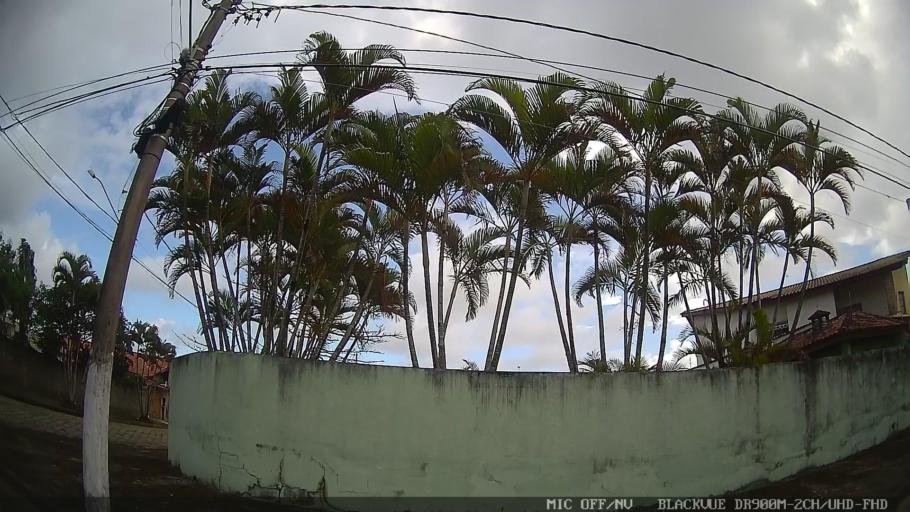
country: BR
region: Sao Paulo
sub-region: Itanhaem
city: Itanhaem
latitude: -24.2179
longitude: -46.8493
